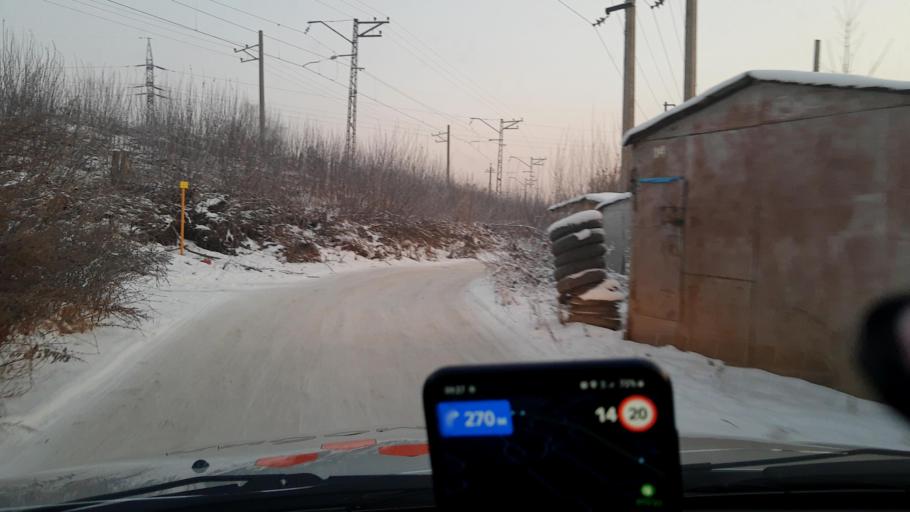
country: RU
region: Bashkortostan
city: Ufa
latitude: 54.8279
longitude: 56.1091
